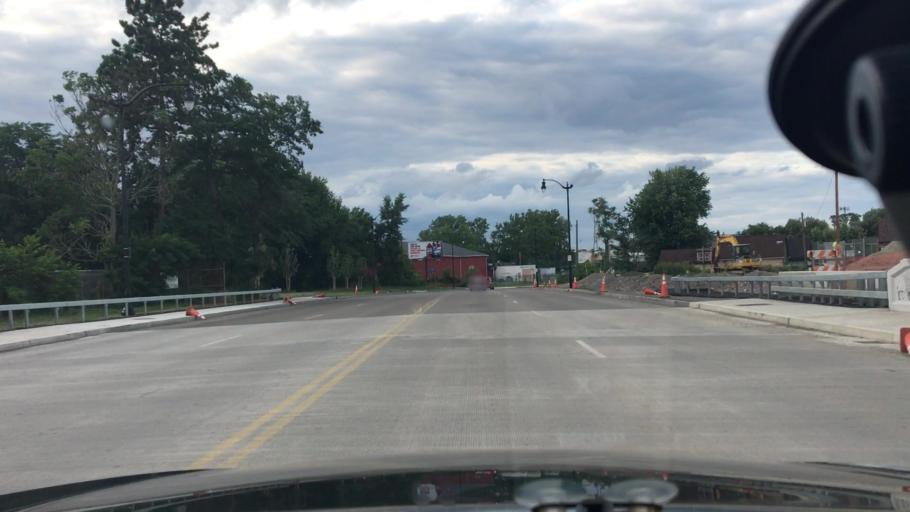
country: US
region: New York
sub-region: Erie County
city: West Seneca
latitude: 42.8623
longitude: -78.8255
